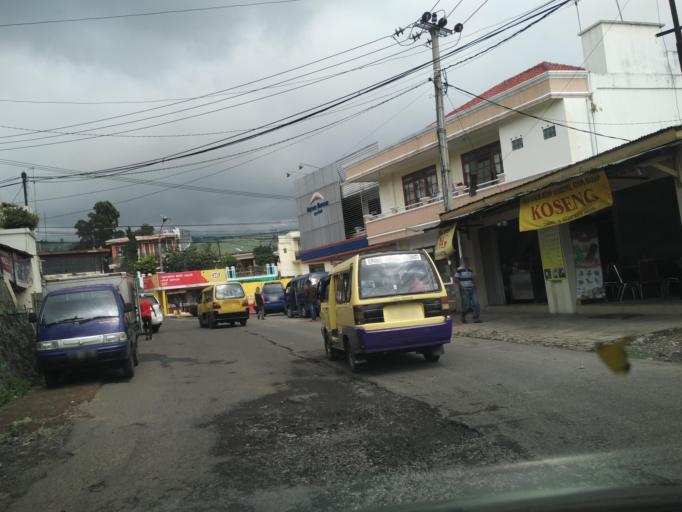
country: ID
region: West Java
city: Sukabumi
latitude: -6.7367
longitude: 107.0439
